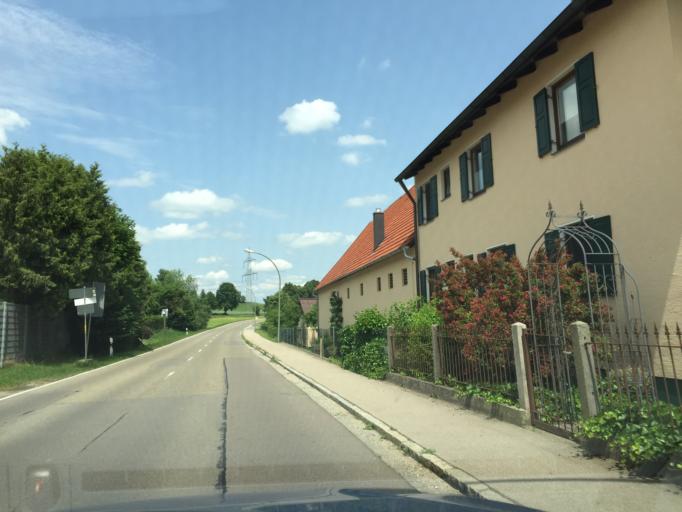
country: DE
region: Bavaria
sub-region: Swabia
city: Zusamaltheim
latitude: 48.5316
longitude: 10.6365
